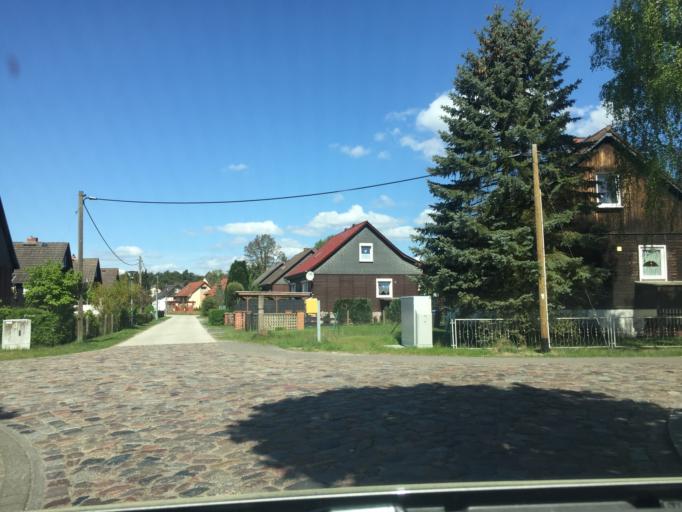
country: DE
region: Mecklenburg-Vorpommern
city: Torgelow
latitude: 53.6190
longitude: 14.0327
